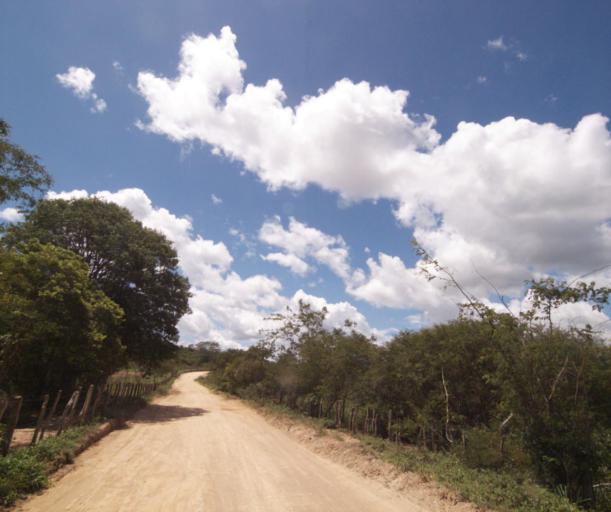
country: BR
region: Bahia
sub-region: Pocoes
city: Pocoes
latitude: -14.3773
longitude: -40.5661
